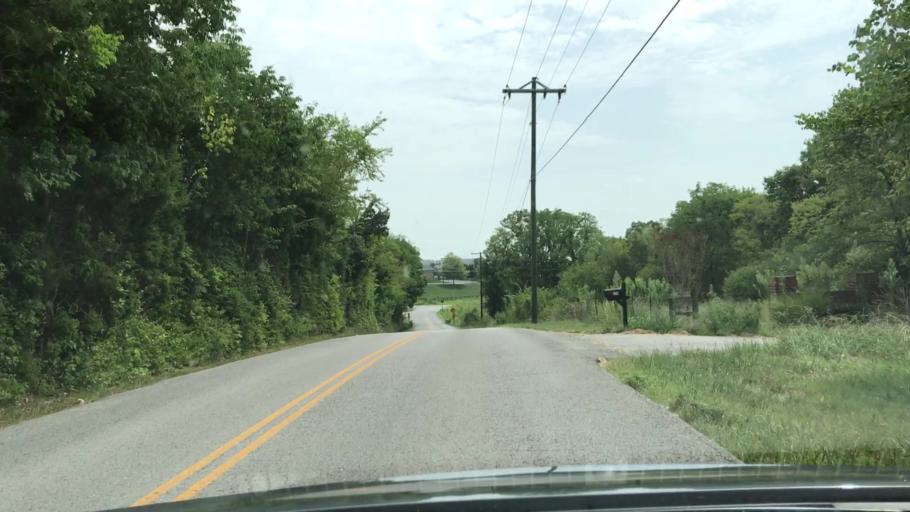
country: US
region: Tennessee
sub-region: Rutherford County
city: La Vergne
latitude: 35.9752
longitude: -86.5830
